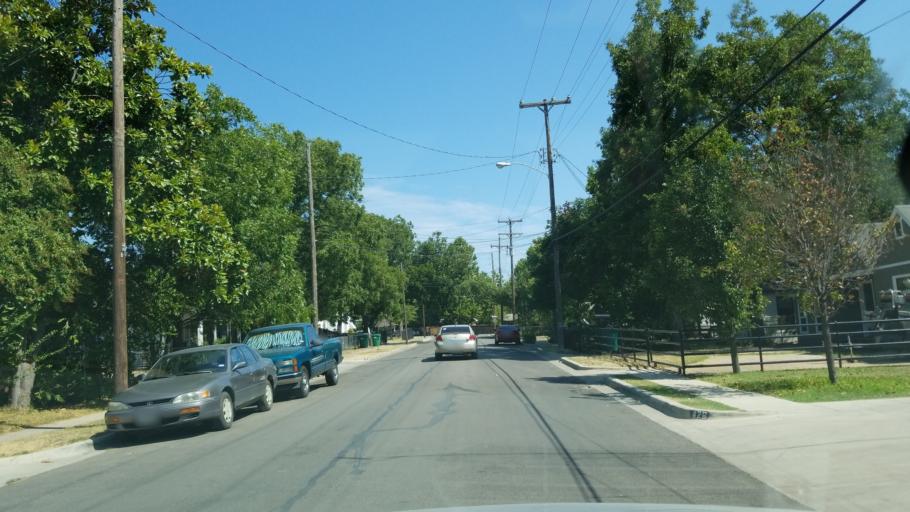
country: US
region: Texas
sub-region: Dallas County
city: Cockrell Hill
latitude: 32.7413
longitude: -96.8886
